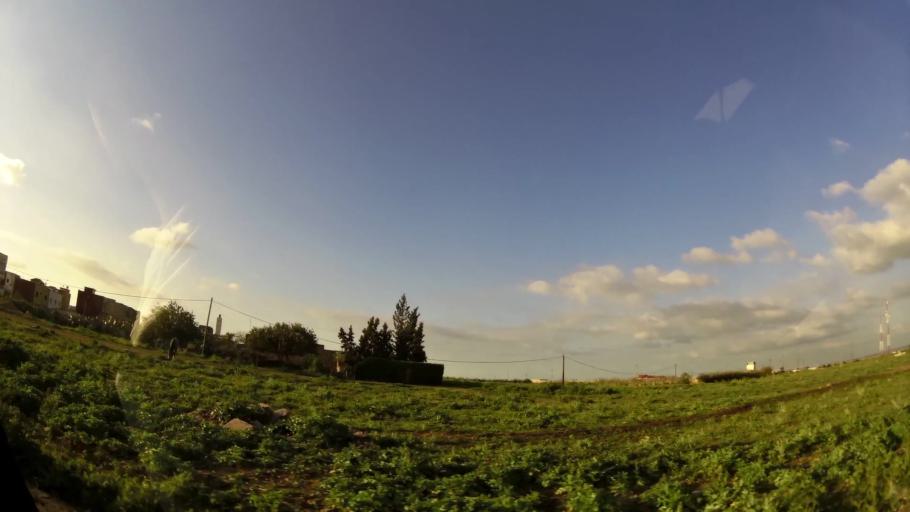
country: MA
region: Chaouia-Ouardigha
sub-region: Settat Province
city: Settat
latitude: 33.0077
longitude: -7.5946
